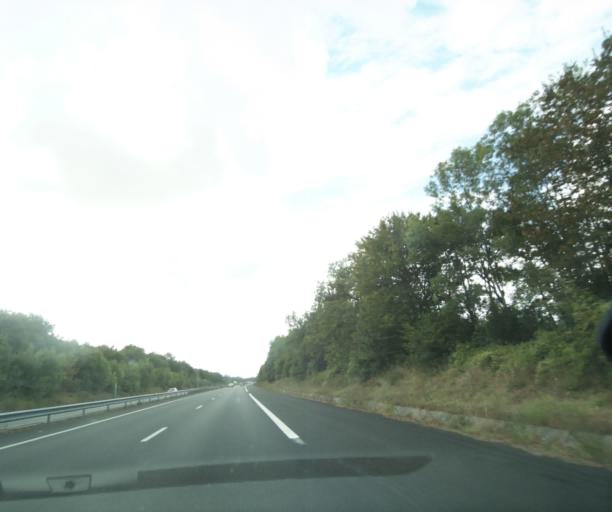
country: FR
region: Poitou-Charentes
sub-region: Departement de la Charente-Maritime
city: Thenac
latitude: 45.6676
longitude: -0.6376
